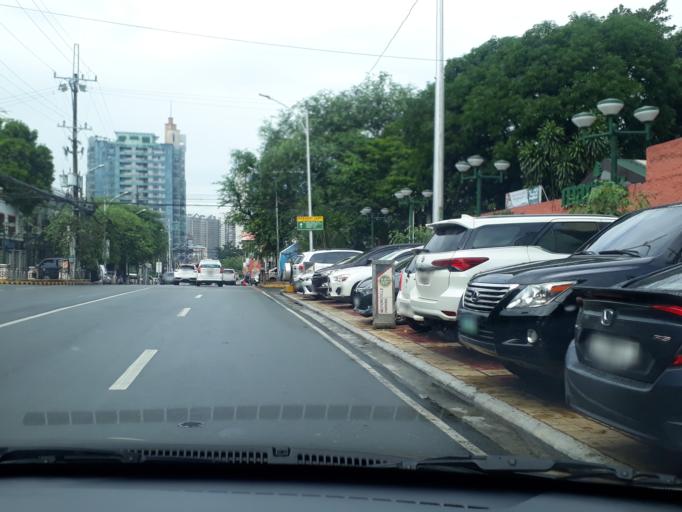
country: PH
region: Calabarzon
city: Del Monte
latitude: 14.6321
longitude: 121.0347
